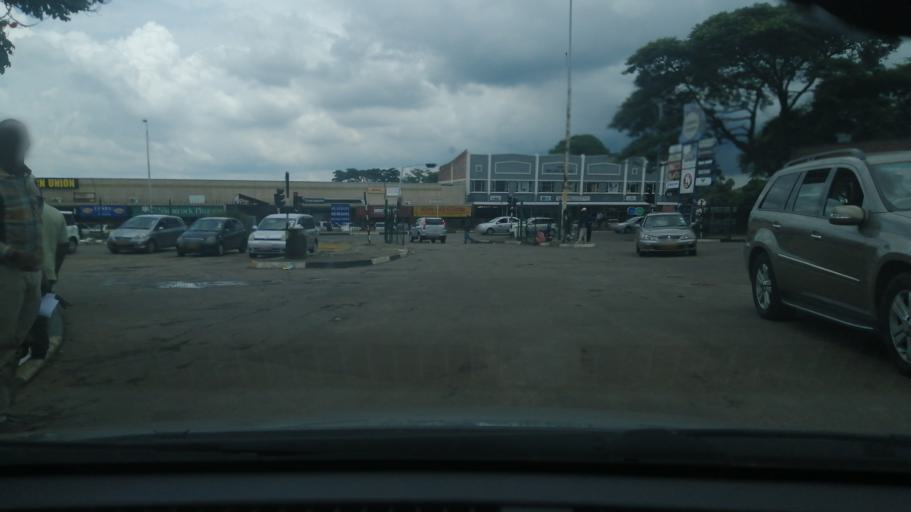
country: ZW
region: Harare
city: Harare
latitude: -17.8031
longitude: 31.0377
